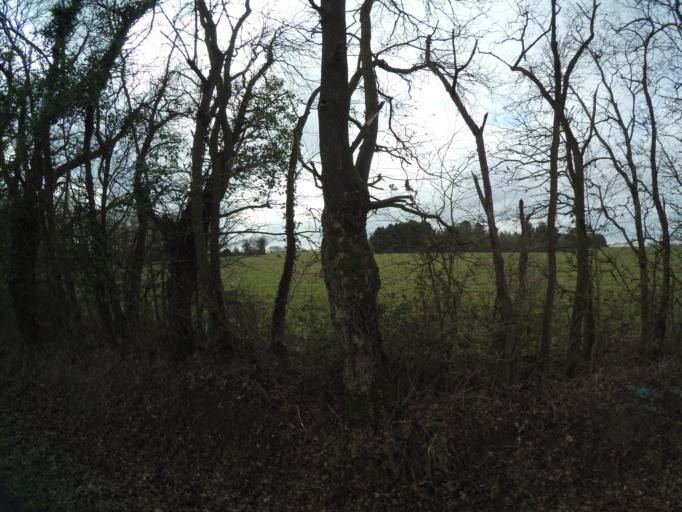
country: FR
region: Pays de la Loire
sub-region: Departement de la Loire-Atlantique
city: Saint-Hilaire-de-Clisson
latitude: 47.0414
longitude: -1.2918
